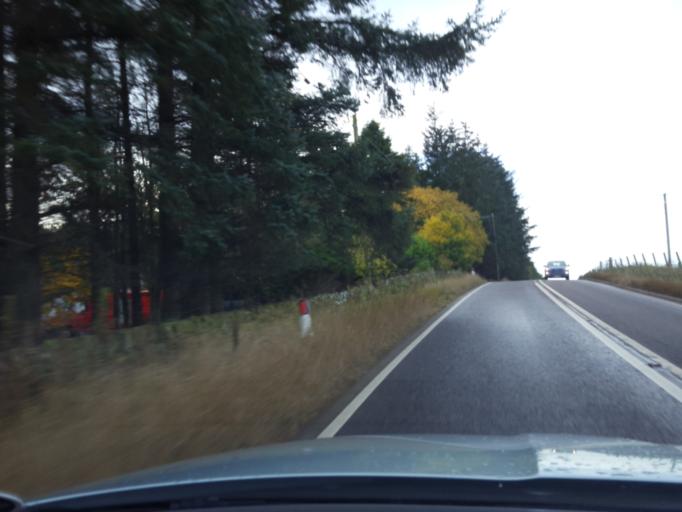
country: GB
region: Scotland
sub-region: South Lanarkshire
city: Carnwath
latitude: 55.7180
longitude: -3.5863
